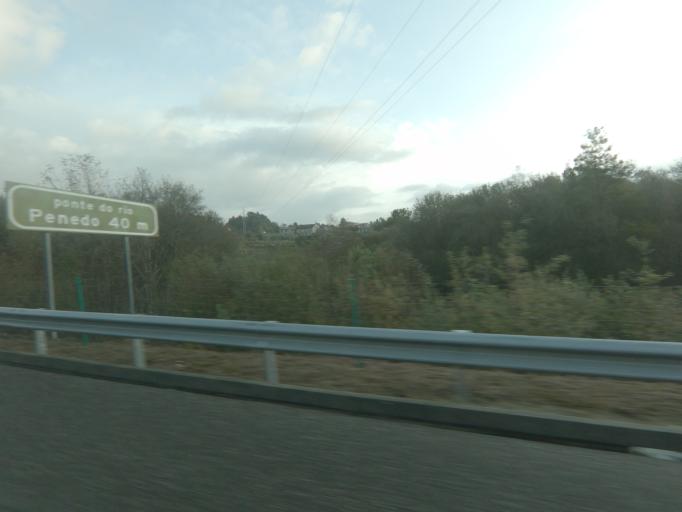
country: ES
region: Galicia
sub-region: Provincia de Pontevedra
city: Tui
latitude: 42.1076
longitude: -8.6499
